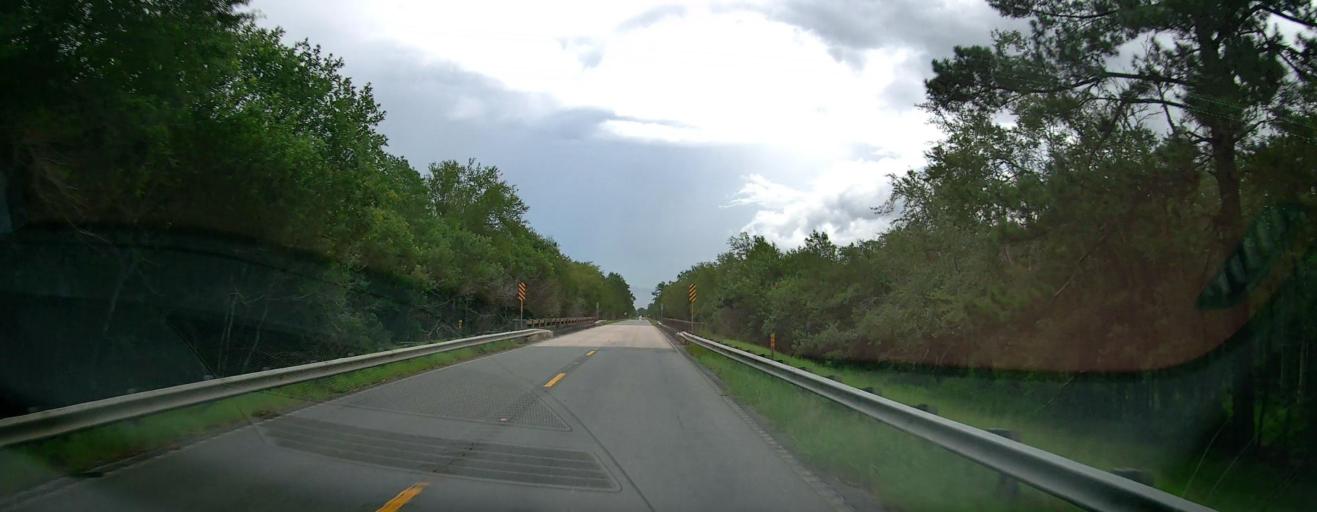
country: US
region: Georgia
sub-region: Pierce County
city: Blackshear
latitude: 31.3614
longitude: -82.0729
